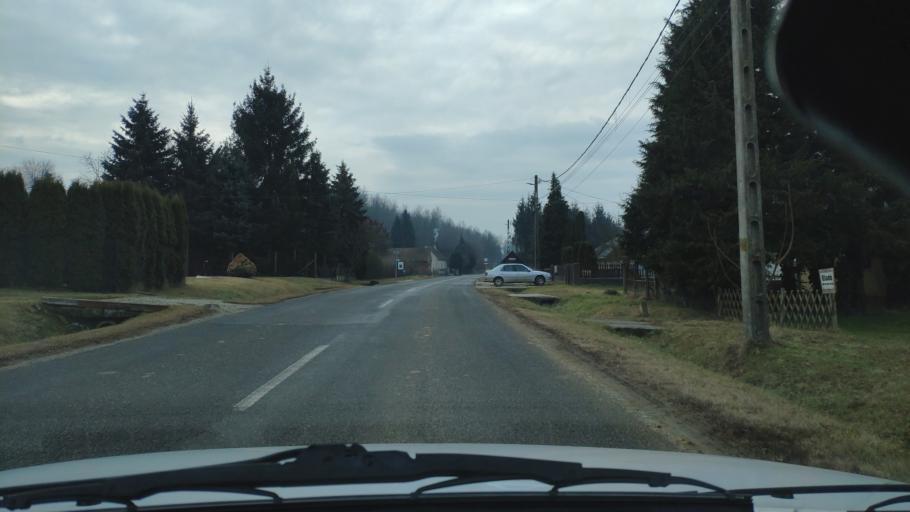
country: HU
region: Zala
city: Nagykanizsa
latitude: 46.5187
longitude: 16.9821
